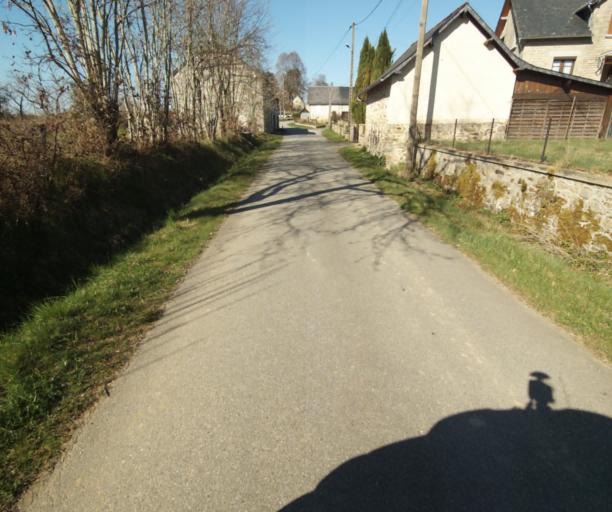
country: FR
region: Limousin
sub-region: Departement de la Correze
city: Chamboulive
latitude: 45.4699
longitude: 1.7347
